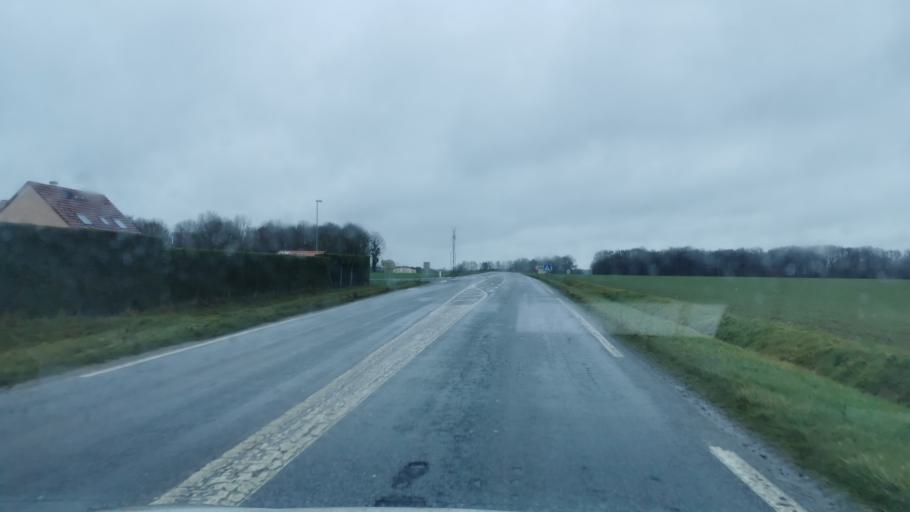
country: FR
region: Haute-Normandie
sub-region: Departement de l'Eure
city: Normanville
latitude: 49.0868
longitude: 1.1790
